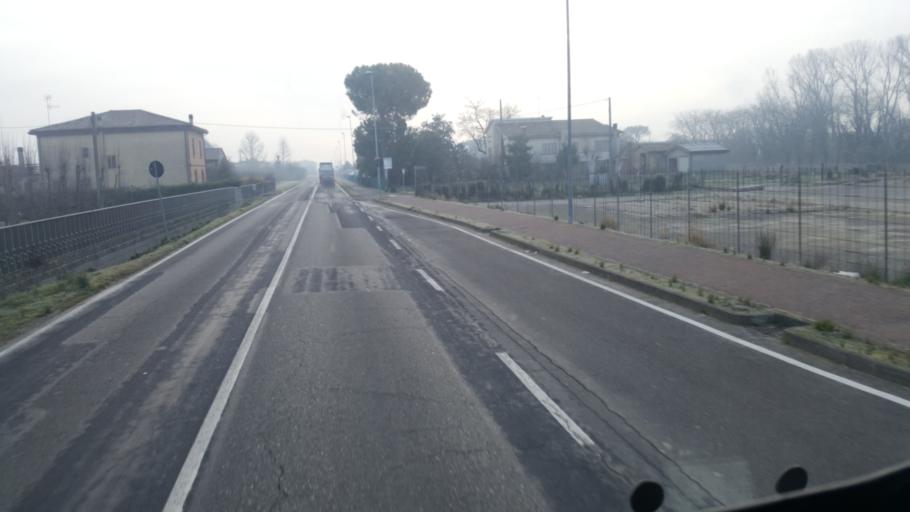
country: IT
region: Emilia-Romagna
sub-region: Provincia di Ravenna
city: Bagnacavallo
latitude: 44.4122
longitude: 11.9878
